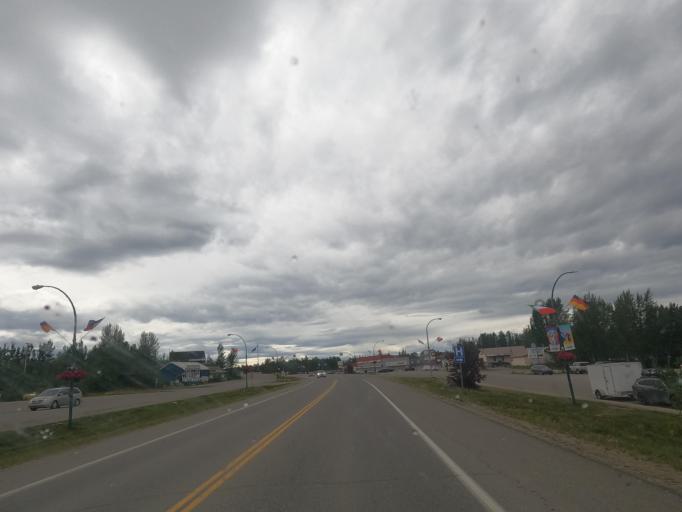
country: CA
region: Yukon
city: Watson Lake
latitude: 60.0624
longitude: -128.7058
